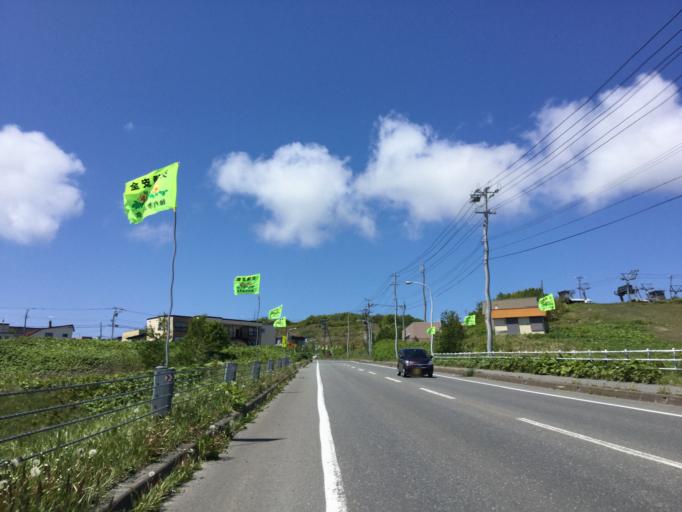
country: JP
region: Hokkaido
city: Wakkanai
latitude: 45.3865
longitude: 141.6889
